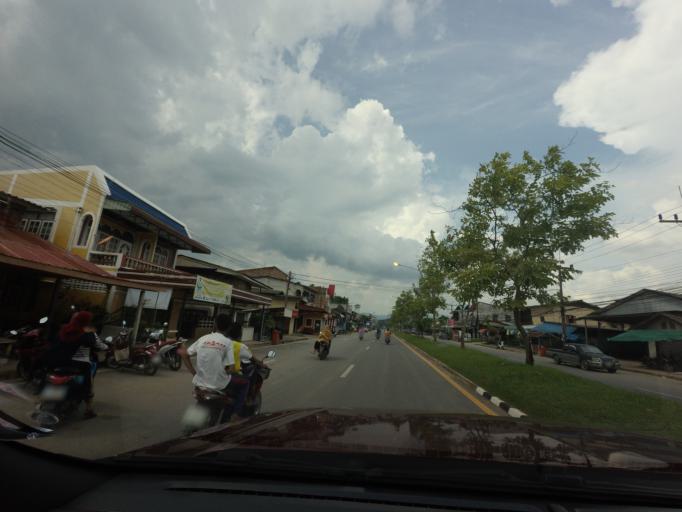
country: TH
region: Yala
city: Ban Nang Sata
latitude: 6.2615
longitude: 101.2566
